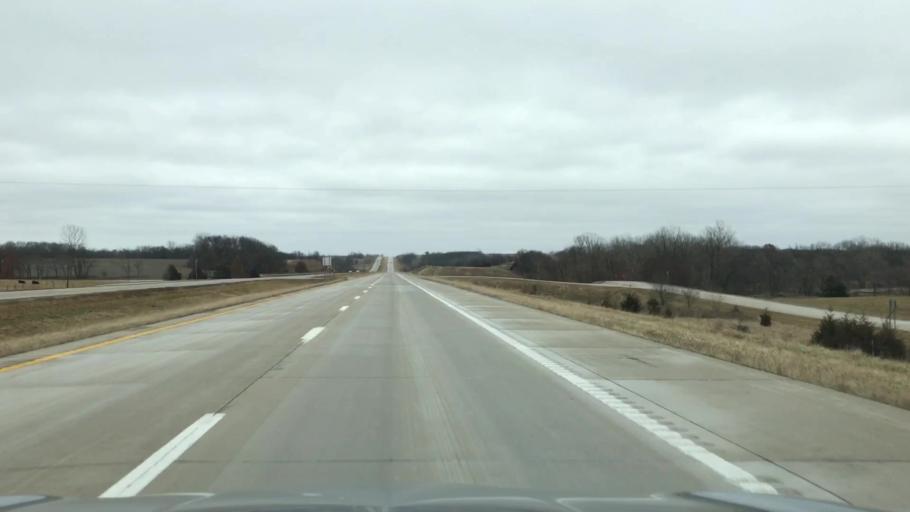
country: US
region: Missouri
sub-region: Livingston County
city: Chillicothe
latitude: 39.7359
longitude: -93.7421
